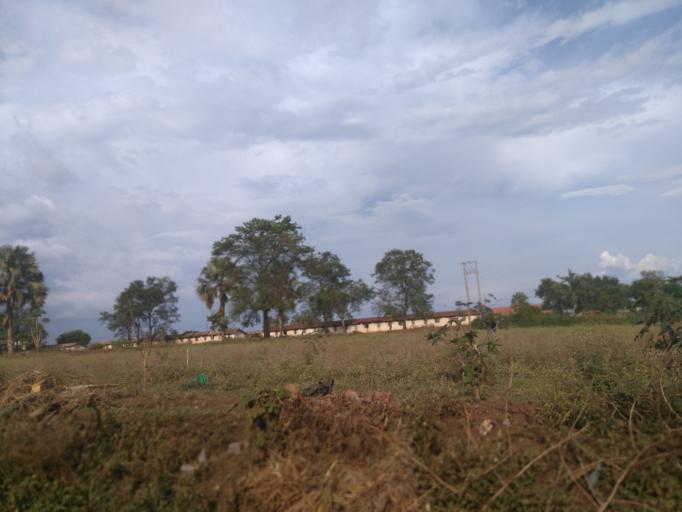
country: UG
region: Eastern Region
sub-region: Jinja District
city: Jinja
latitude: 0.4157
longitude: 33.2149
